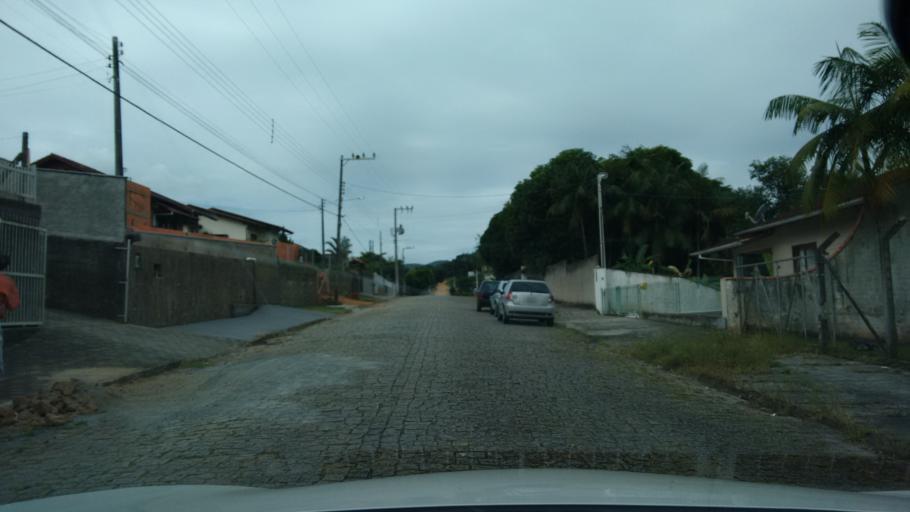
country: BR
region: Santa Catarina
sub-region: Timbo
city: Timbo
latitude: -26.8122
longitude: -49.2683
